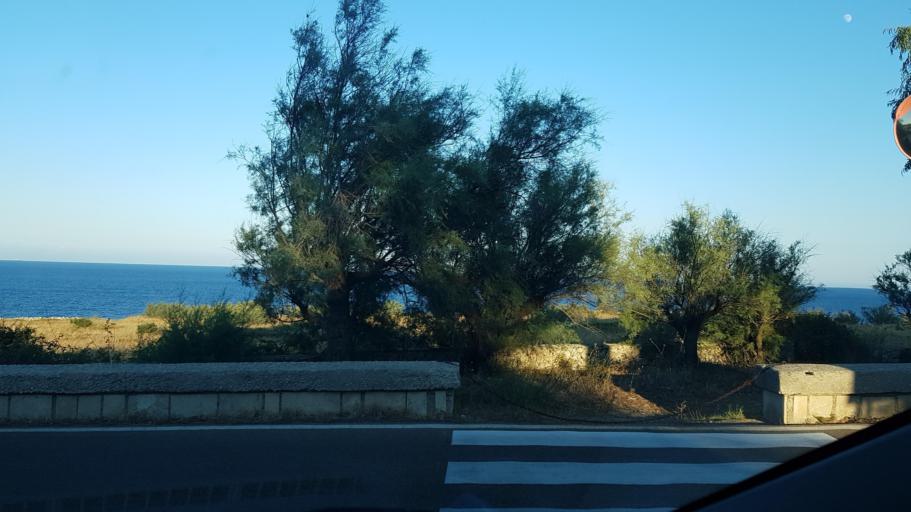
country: IT
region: Apulia
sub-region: Provincia di Lecce
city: Cerfignano
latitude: 40.0751
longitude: 18.4816
